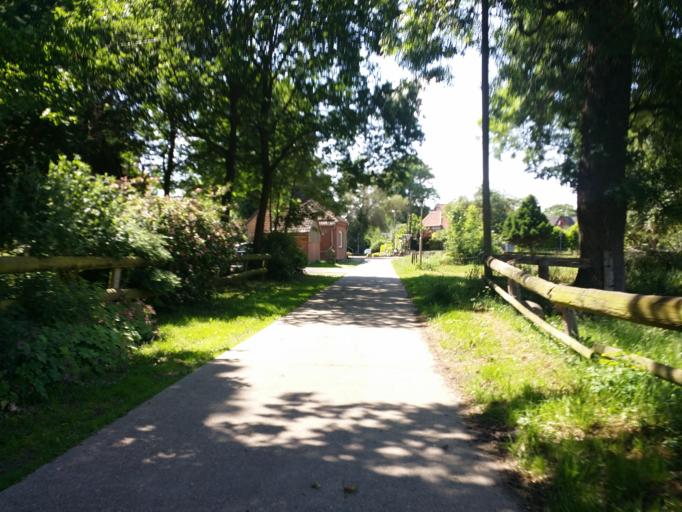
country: DE
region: Lower Saxony
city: Lemwerder
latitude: 53.1418
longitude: 8.5761
